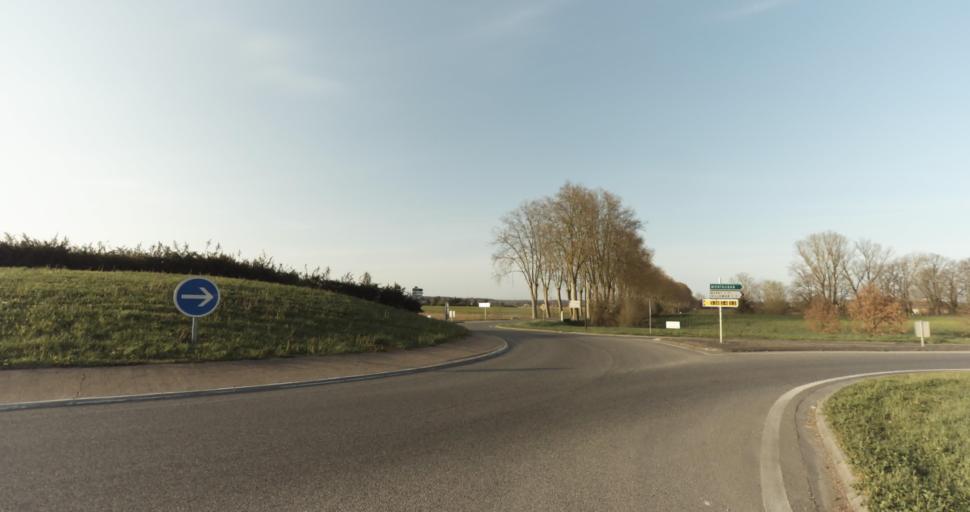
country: FR
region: Midi-Pyrenees
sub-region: Departement de la Haute-Garonne
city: Buzet-sur-Tarn
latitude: 43.7712
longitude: 1.6554
